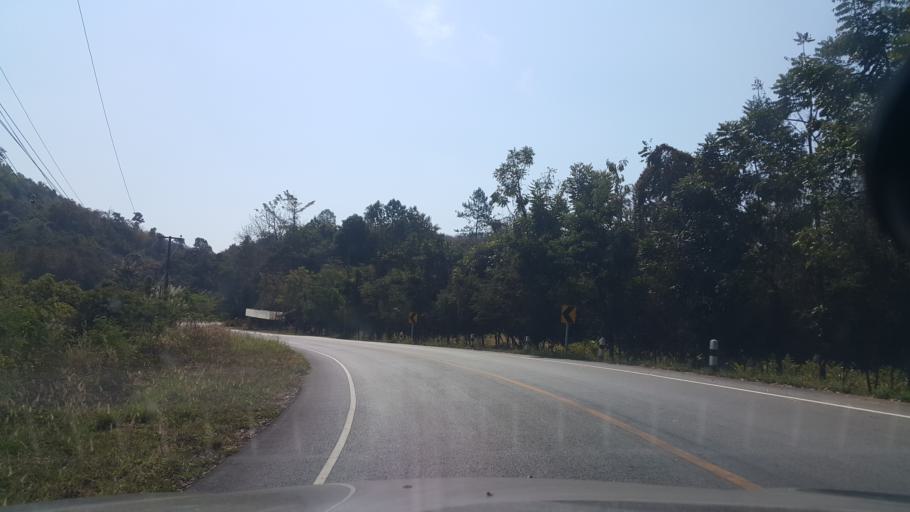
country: TH
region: Changwat Udon Thani
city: Na Yung
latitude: 17.9306
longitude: 102.0753
